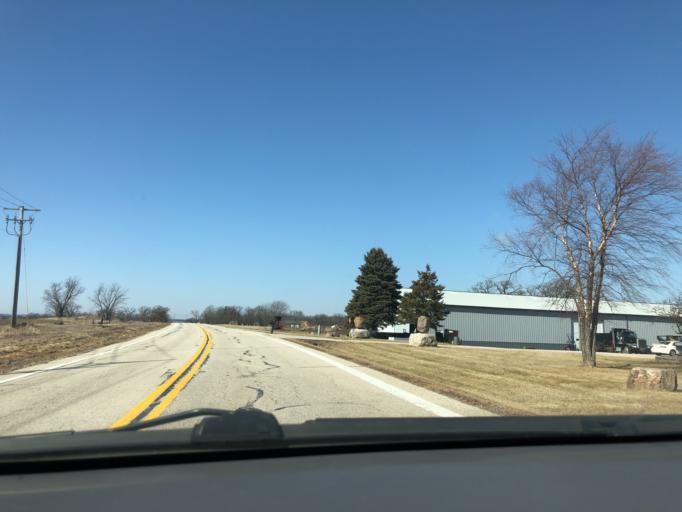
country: US
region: Illinois
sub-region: Kane County
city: Hampshire
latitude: 42.1271
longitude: -88.5154
